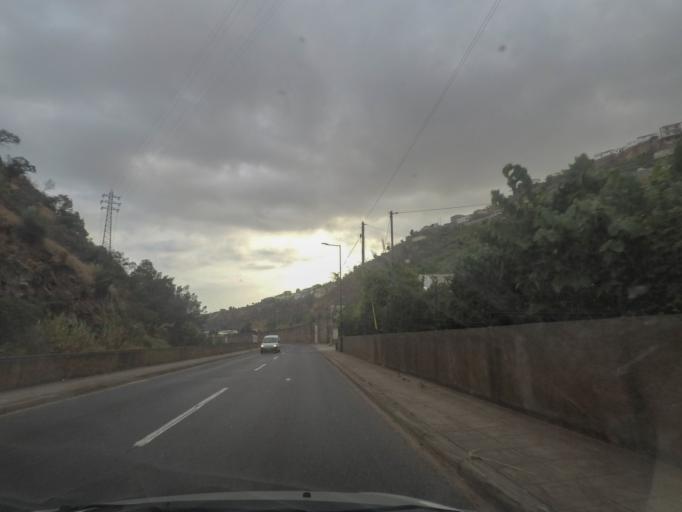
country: PT
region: Madeira
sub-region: Funchal
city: Nossa Senhora do Monte
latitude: 32.6691
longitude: -16.9185
